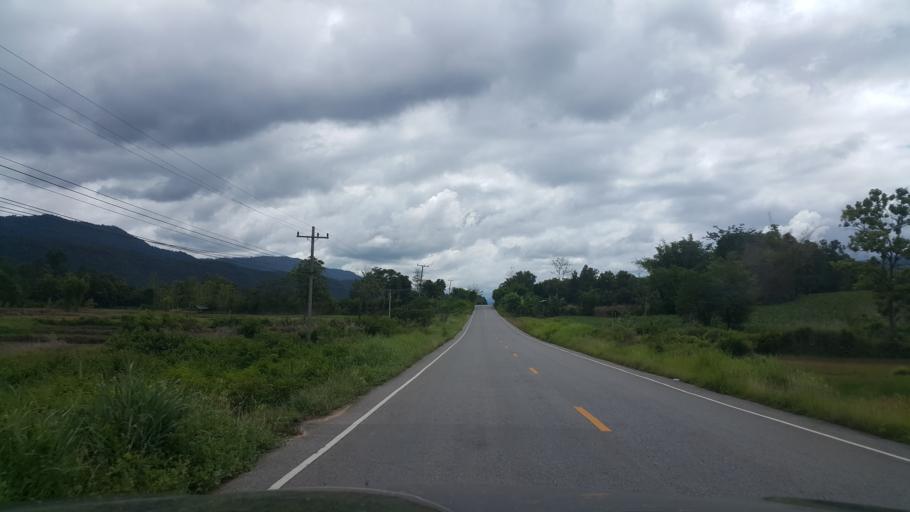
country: TH
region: Phitsanulok
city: Chat Trakan
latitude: 17.2943
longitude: 100.6513
